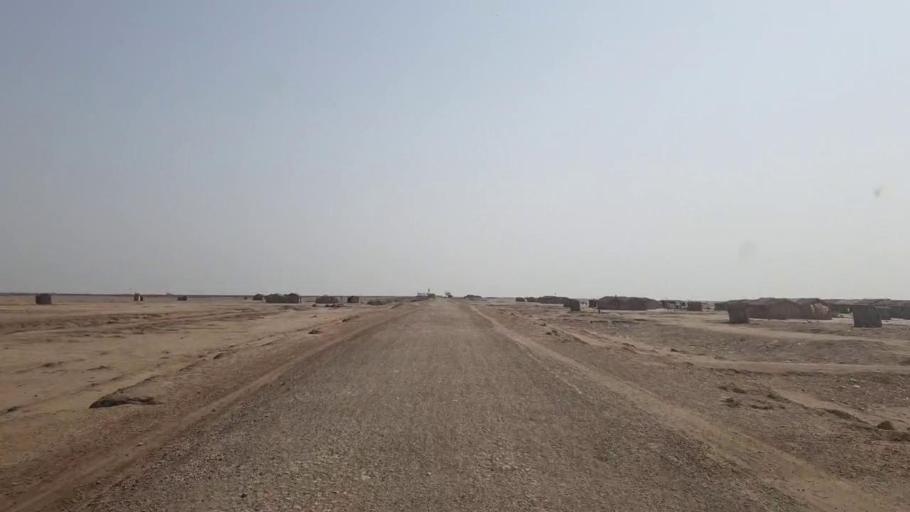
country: PK
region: Sindh
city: Jati
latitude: 24.3372
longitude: 68.5993
